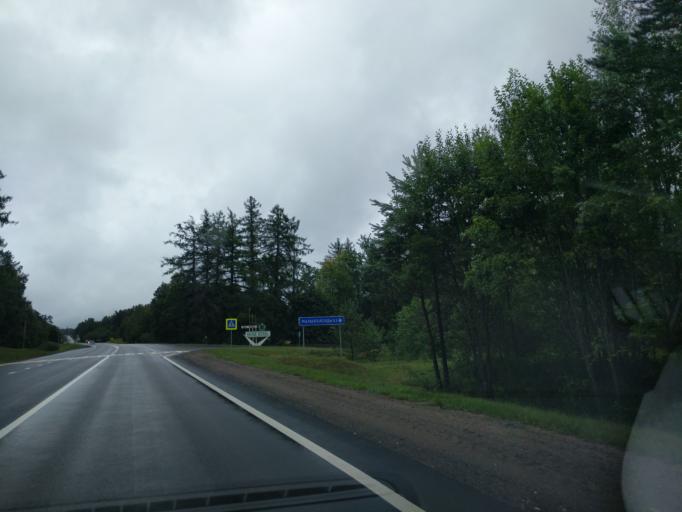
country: BY
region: Minsk
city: Syomkava
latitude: 54.2327
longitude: 27.4845
